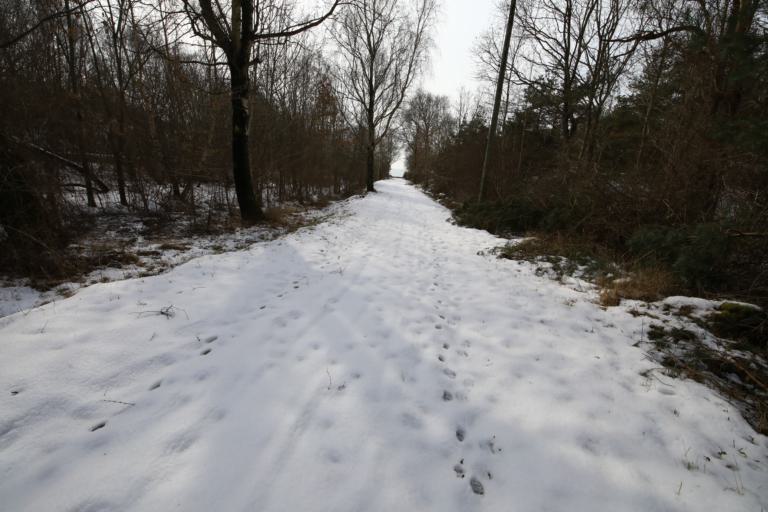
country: SE
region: Halland
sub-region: Kungsbacka Kommun
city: Frillesas
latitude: 57.2169
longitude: 12.1696
